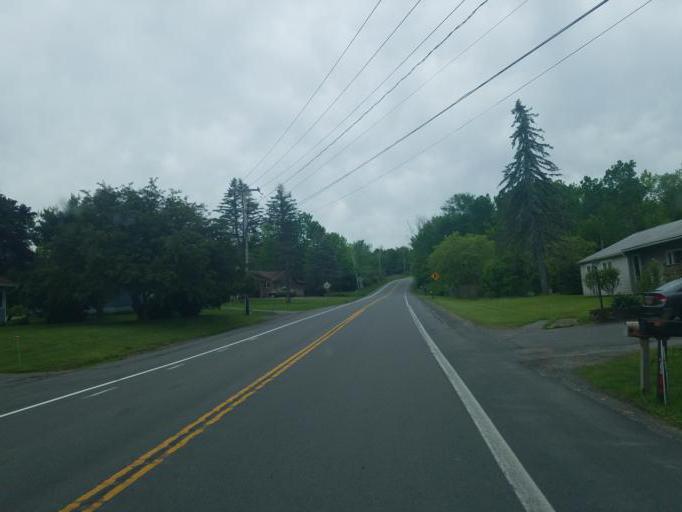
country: US
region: New York
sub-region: Herkimer County
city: Mohawk
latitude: 42.9951
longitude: -75.0083
